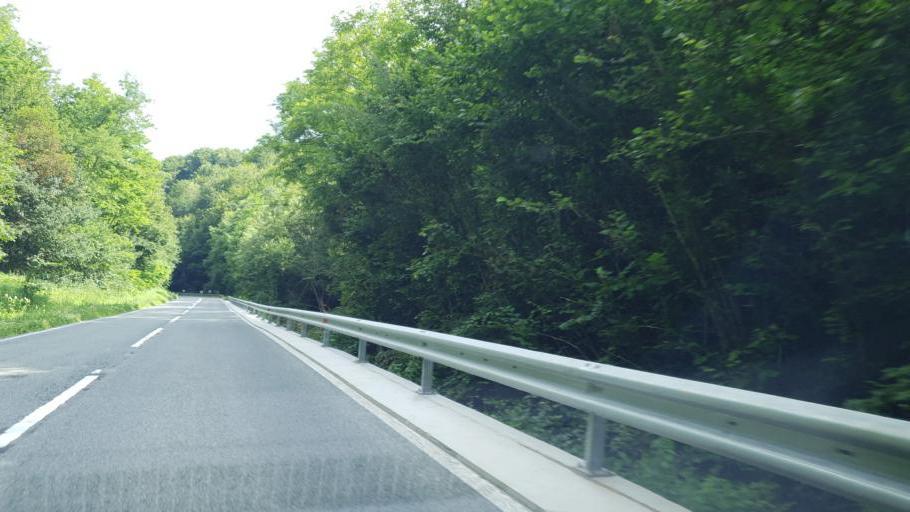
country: SI
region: Ilirska Bistrica
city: Ilirska Bistrica
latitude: 45.5178
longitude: 14.2520
